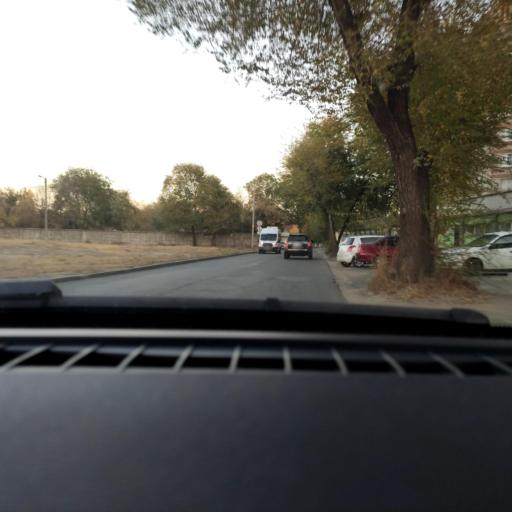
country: RU
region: Voronezj
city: Voronezh
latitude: 51.6841
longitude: 39.2692
